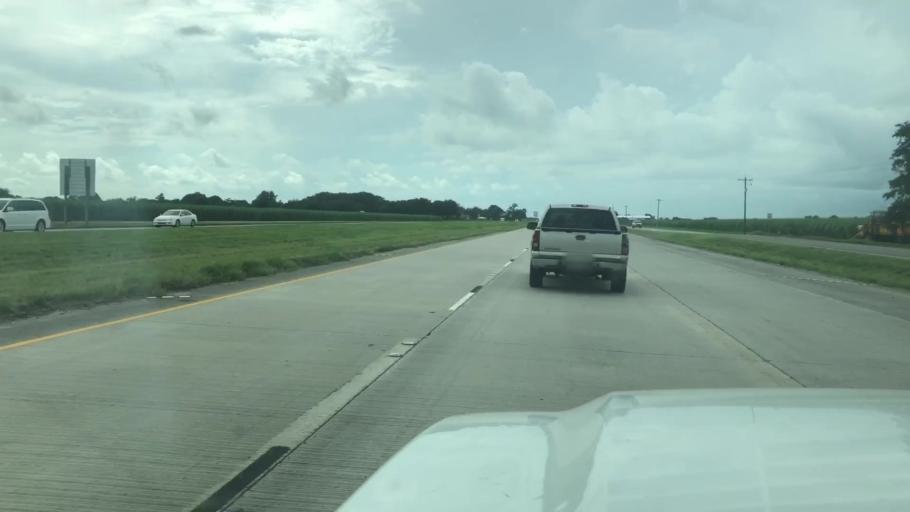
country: US
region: Louisiana
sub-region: Iberia Parish
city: Jeanerette
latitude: 29.9231
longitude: -91.7335
